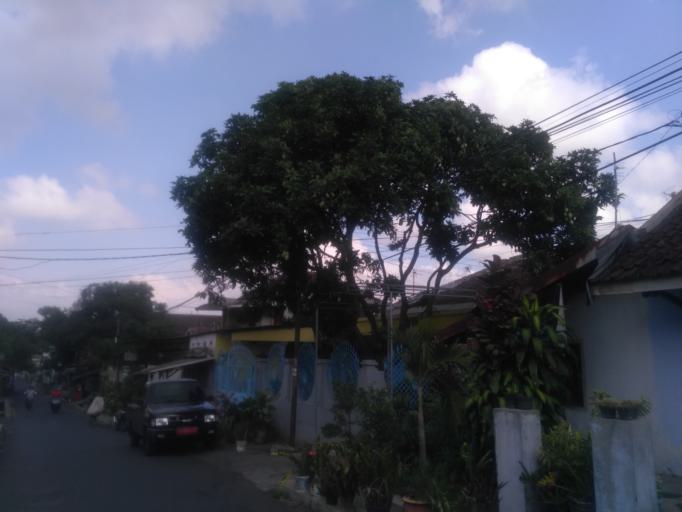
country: ID
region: East Java
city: Malang
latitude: -7.9432
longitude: 112.6352
